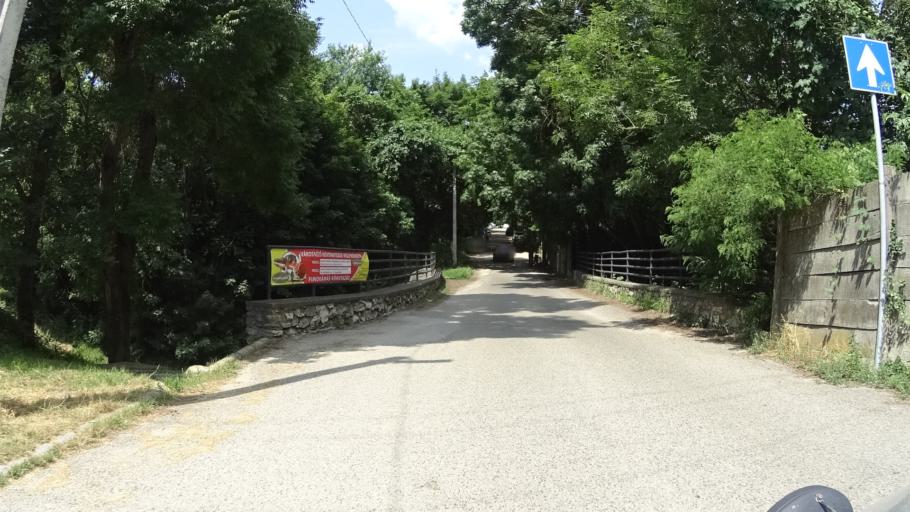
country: HU
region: Veszprem
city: Veszprem
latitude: 47.0884
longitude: 17.8967
